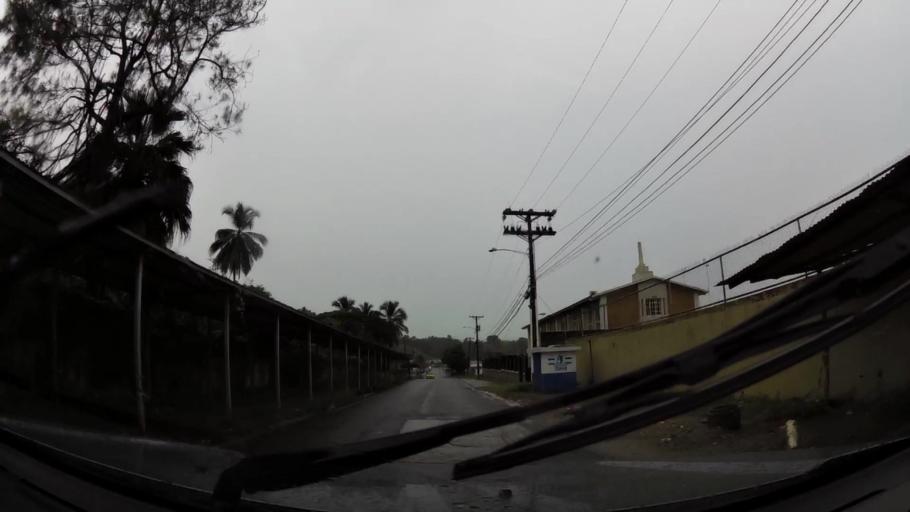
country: PA
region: Colon
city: Sabanitas
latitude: 9.3512
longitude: -79.8044
